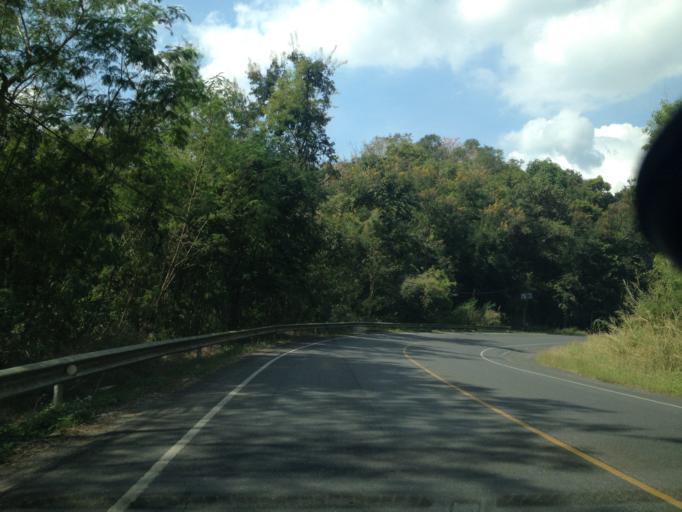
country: TH
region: Chiang Mai
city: Hang Dong
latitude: 18.7550
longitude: 98.8815
